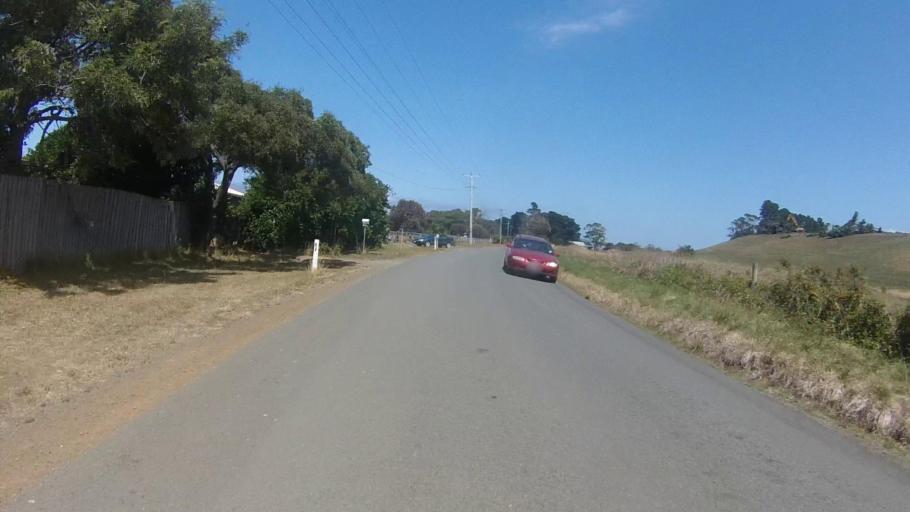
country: AU
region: Tasmania
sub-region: Sorell
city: Sorell
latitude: -42.8215
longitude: 147.8593
